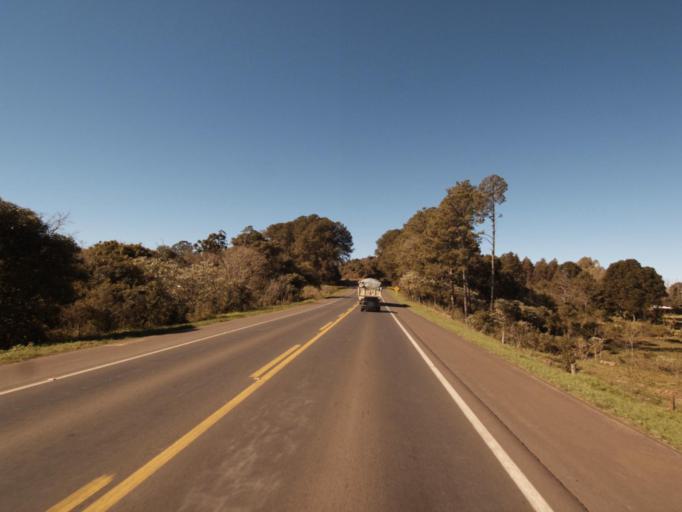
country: BR
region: Santa Catarina
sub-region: Xanxere
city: Xanxere
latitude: -26.9148
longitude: -52.4802
